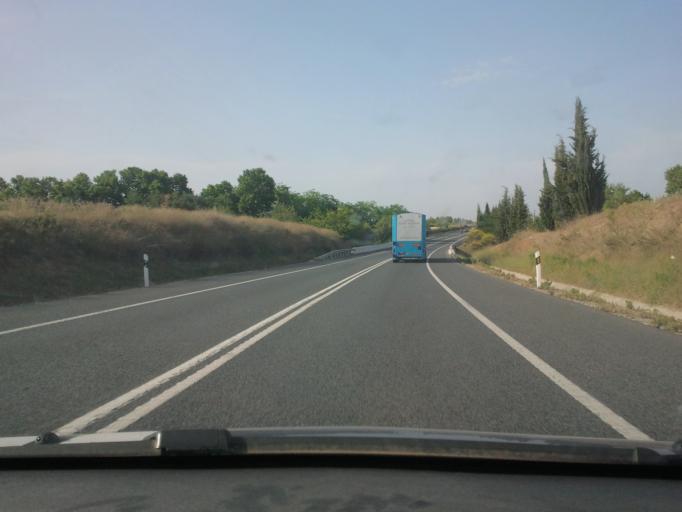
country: ES
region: Catalonia
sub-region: Provincia de Barcelona
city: Castellet
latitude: 41.3169
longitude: 1.6413
